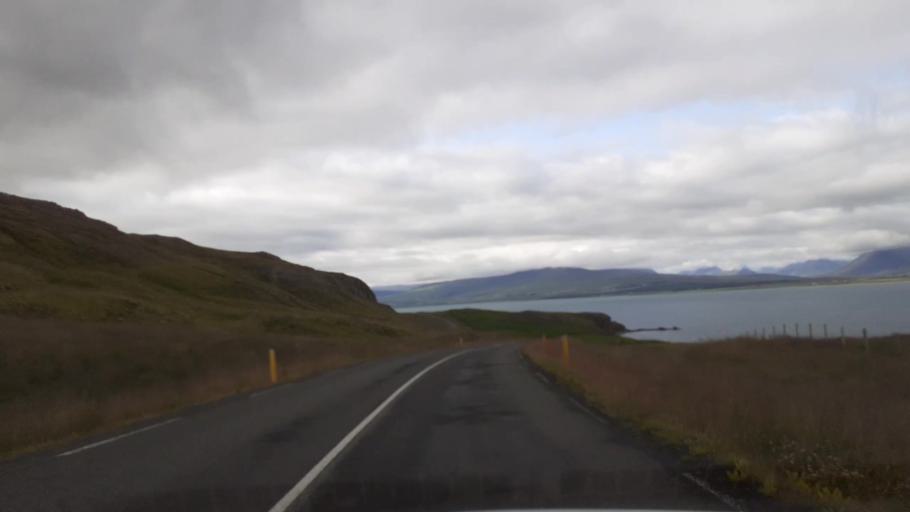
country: IS
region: Northeast
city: Akureyri
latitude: 65.8146
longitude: -18.0493
